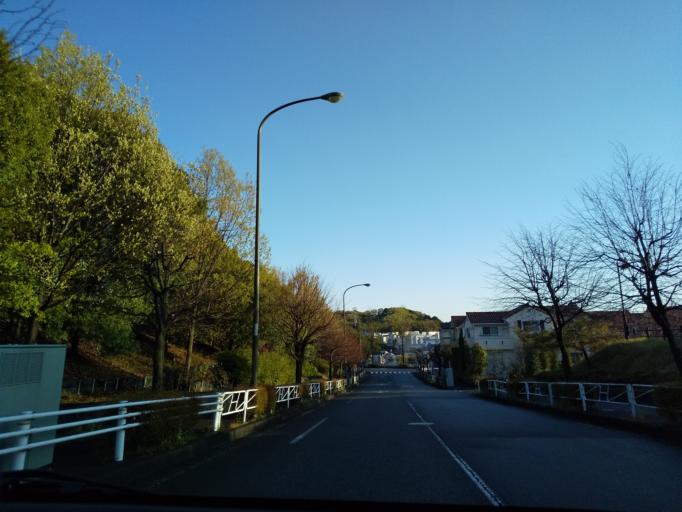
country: JP
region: Tokyo
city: Hachioji
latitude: 35.6132
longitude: 139.3607
